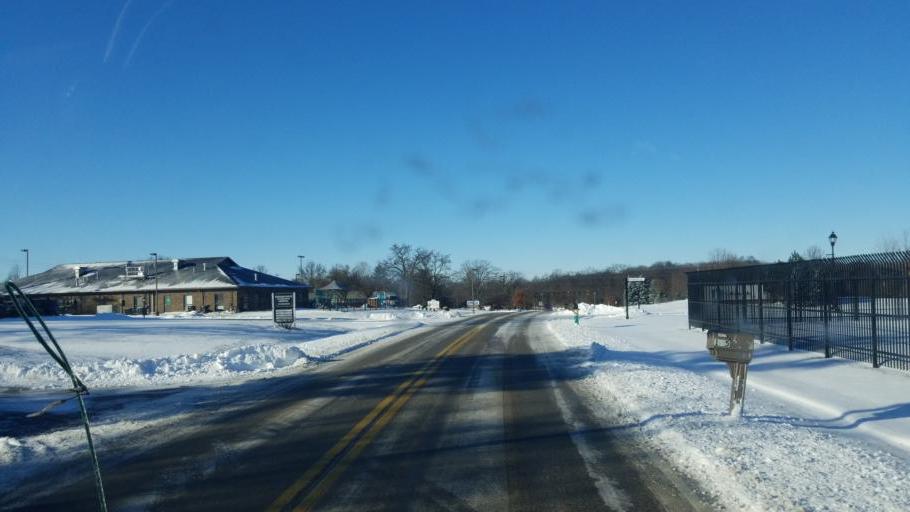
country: US
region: Ohio
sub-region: Delaware County
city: Lewis Center
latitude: 40.1531
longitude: -83.0153
